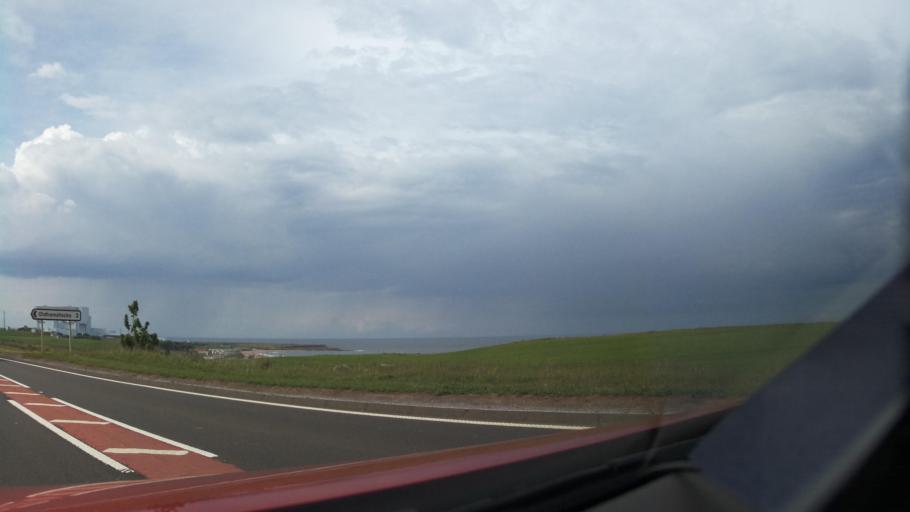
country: GB
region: Scotland
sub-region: East Lothian
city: Dunbar
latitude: 55.9550
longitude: -2.3935
